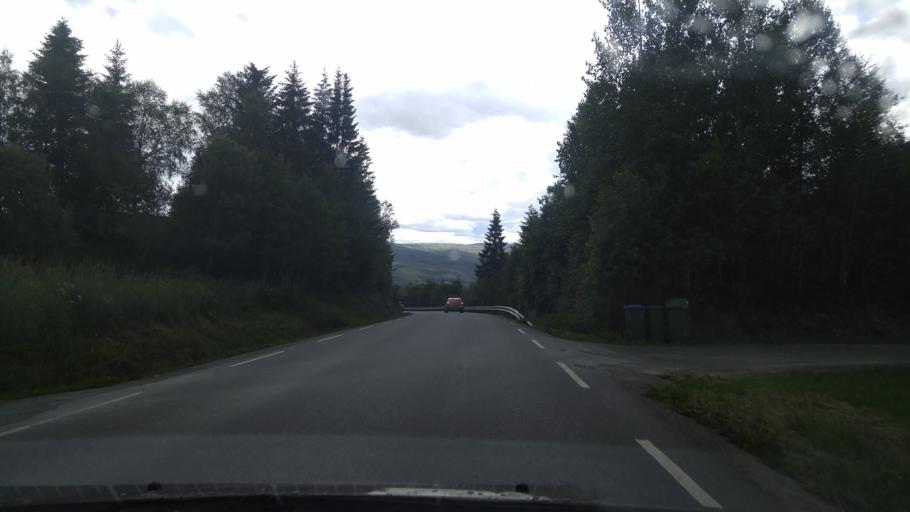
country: NO
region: Nord-Trondelag
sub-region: Levanger
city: Skogn
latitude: 63.6426
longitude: 11.2456
